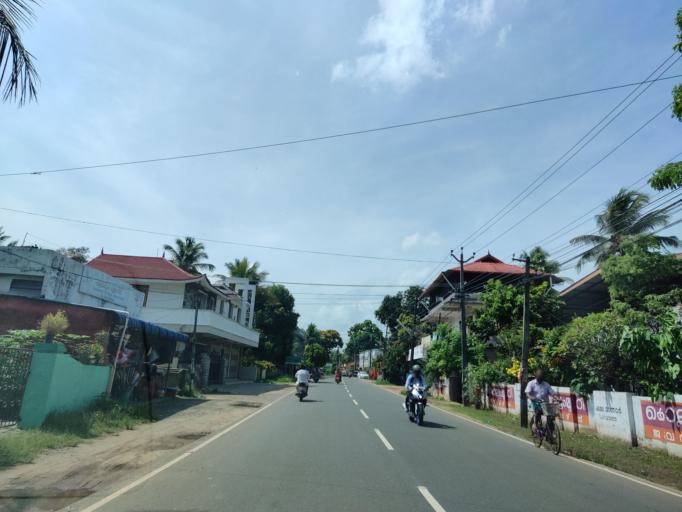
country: IN
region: Kerala
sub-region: Alappuzha
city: Mavelikara
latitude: 9.3046
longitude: 76.5342
